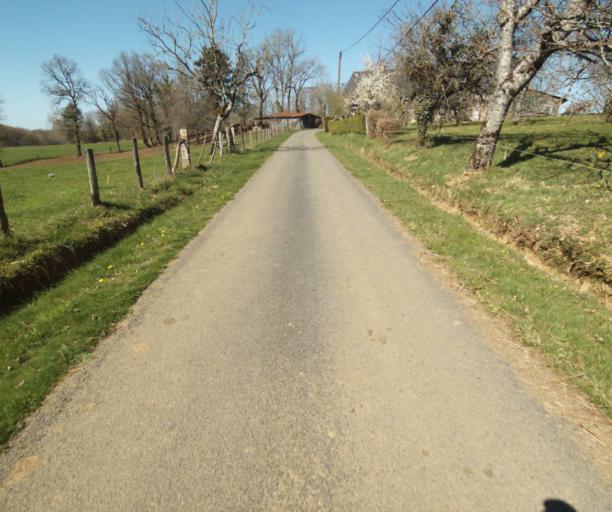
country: FR
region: Limousin
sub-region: Departement de la Correze
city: Chamboulive
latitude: 45.3952
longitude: 1.6810
